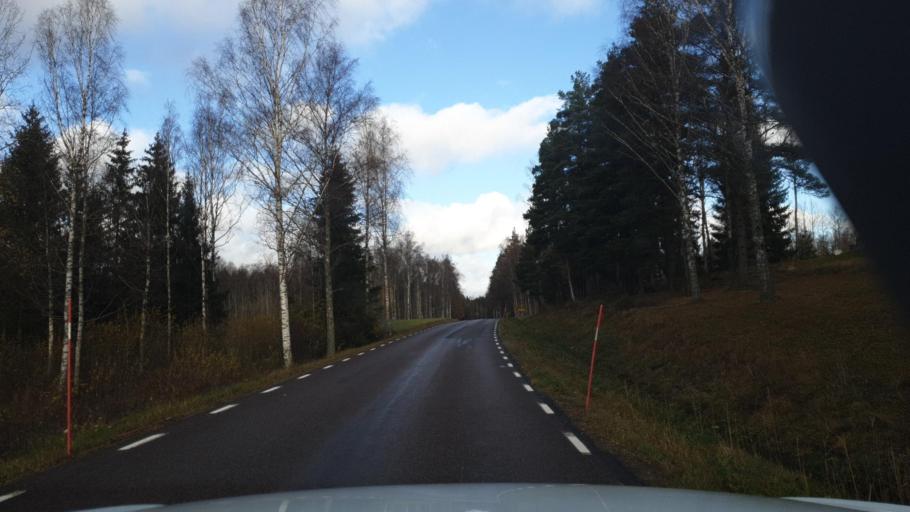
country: SE
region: Vaermland
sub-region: Grums Kommun
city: Slottsbron
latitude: 59.4809
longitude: 12.8837
